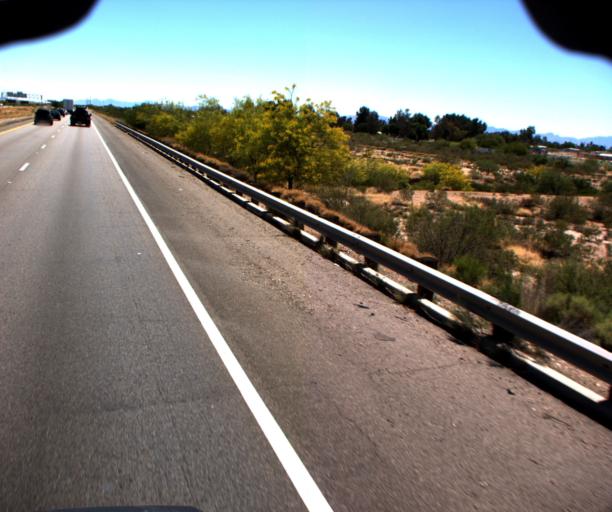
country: US
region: Arizona
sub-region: Pima County
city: Tucson
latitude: 32.1567
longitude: -110.9086
